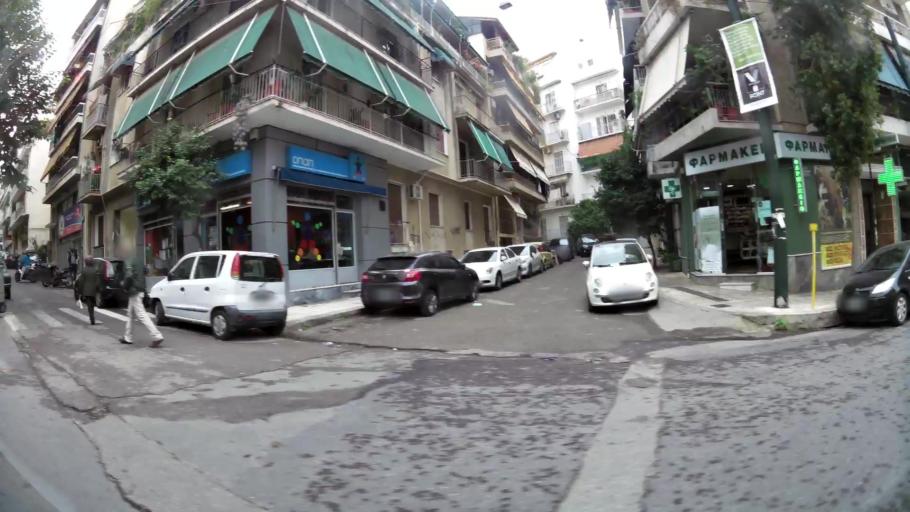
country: GR
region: Attica
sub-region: Nomarchia Athinas
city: Vyronas
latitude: 37.9642
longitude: 23.7530
